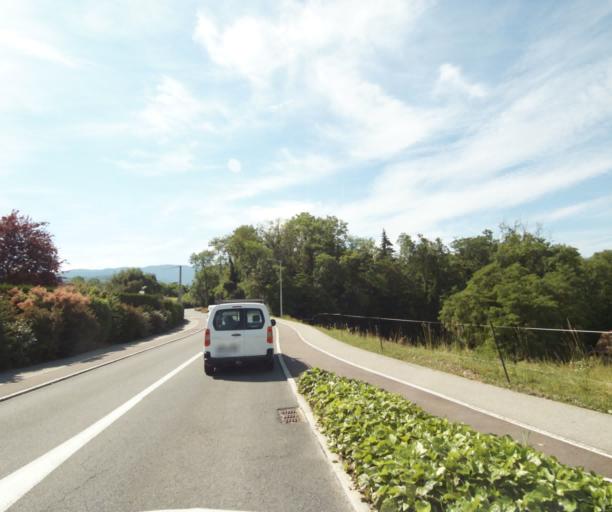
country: FR
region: Rhone-Alpes
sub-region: Departement de la Haute-Savoie
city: Margencel
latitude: 46.3400
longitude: 6.4158
